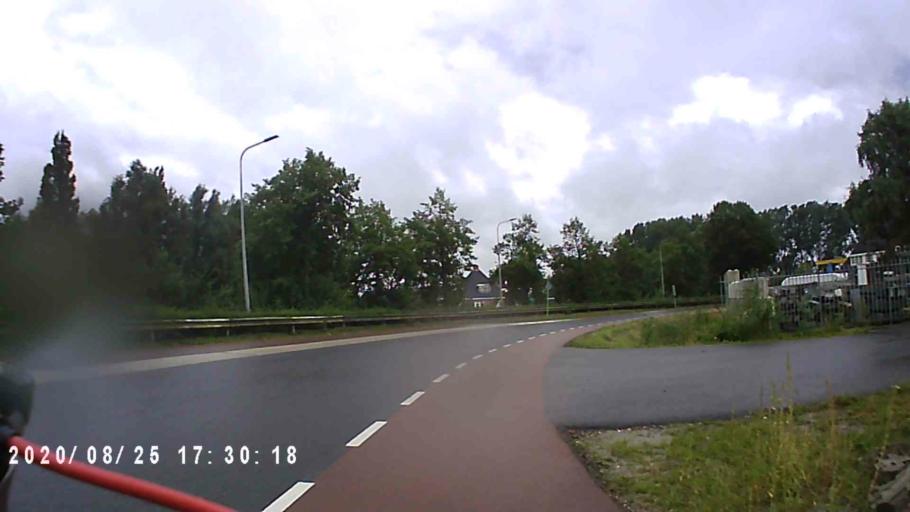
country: NL
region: Groningen
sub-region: Gemeente Zuidhorn
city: Aduard
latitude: 53.2127
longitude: 6.4892
